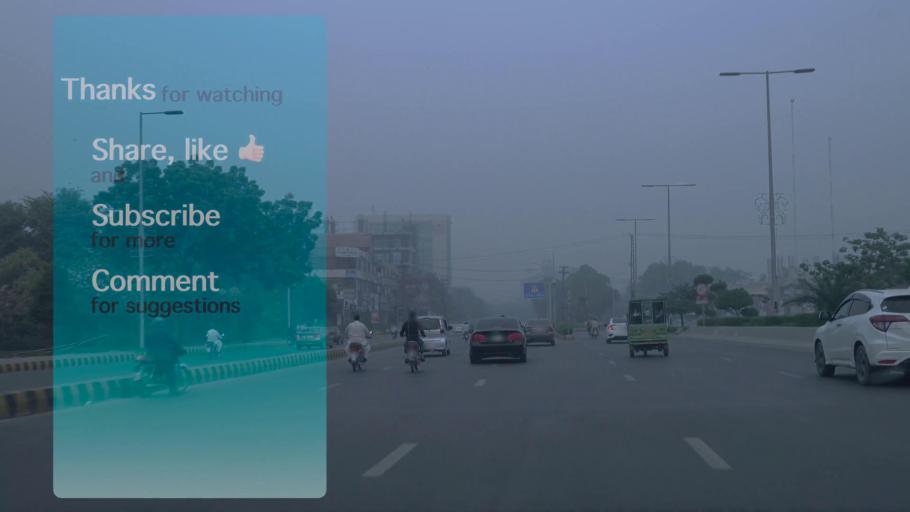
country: PK
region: Punjab
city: Lahore
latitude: 31.5058
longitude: 74.3350
